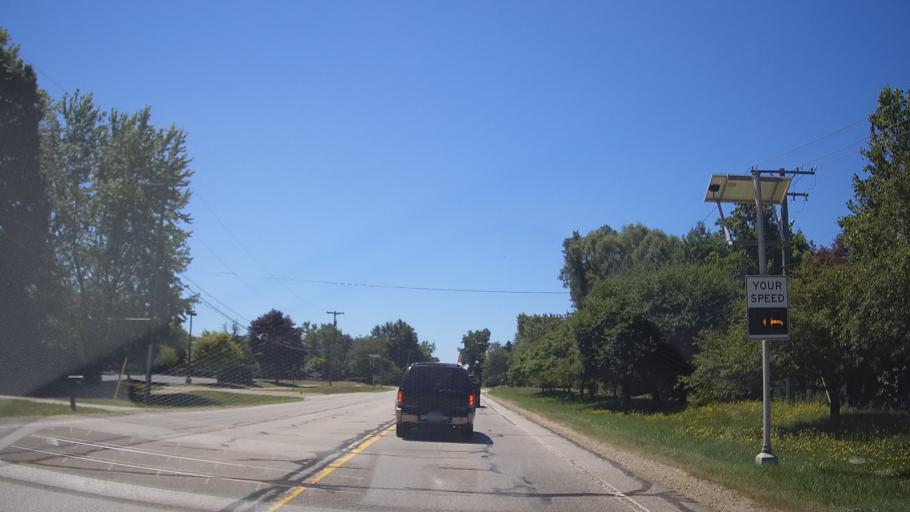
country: US
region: Michigan
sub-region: Oakland County
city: Rochester Hills
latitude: 42.6433
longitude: -83.1120
